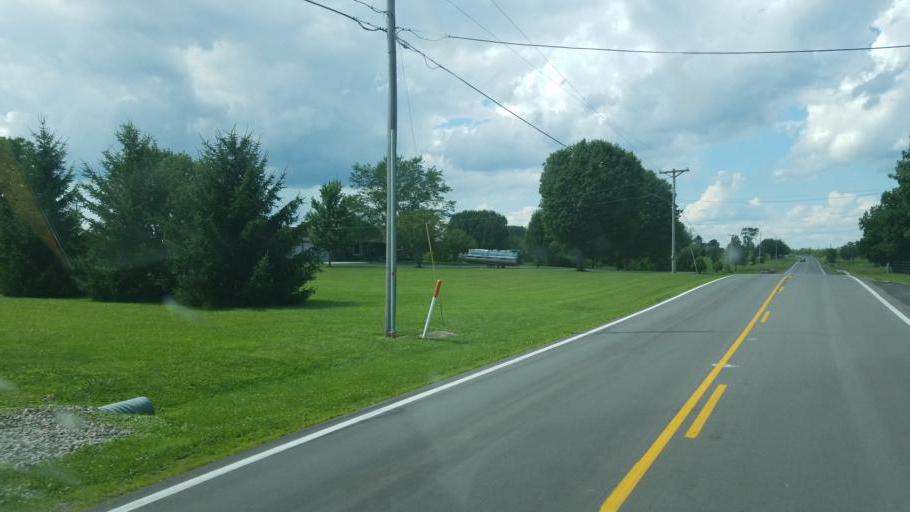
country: US
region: Ohio
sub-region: Highland County
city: Greenfield
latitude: 39.3708
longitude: -83.3789
